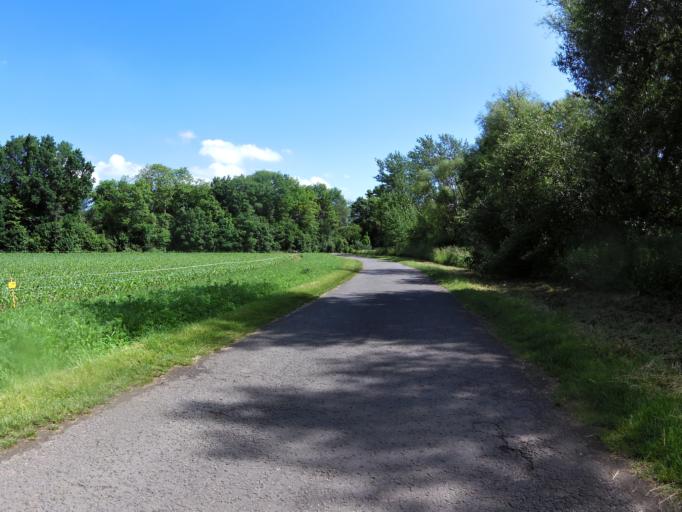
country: DE
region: Hesse
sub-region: Regierungsbezirk Kassel
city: Bad Hersfeld
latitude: 50.8547
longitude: 9.6953
